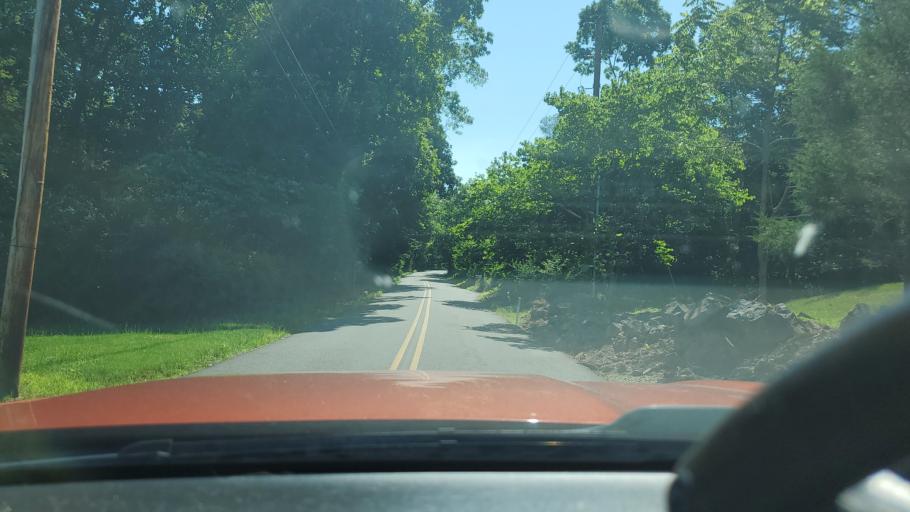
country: US
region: Pennsylvania
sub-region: Montgomery County
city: Red Hill
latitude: 40.3375
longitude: -75.5132
